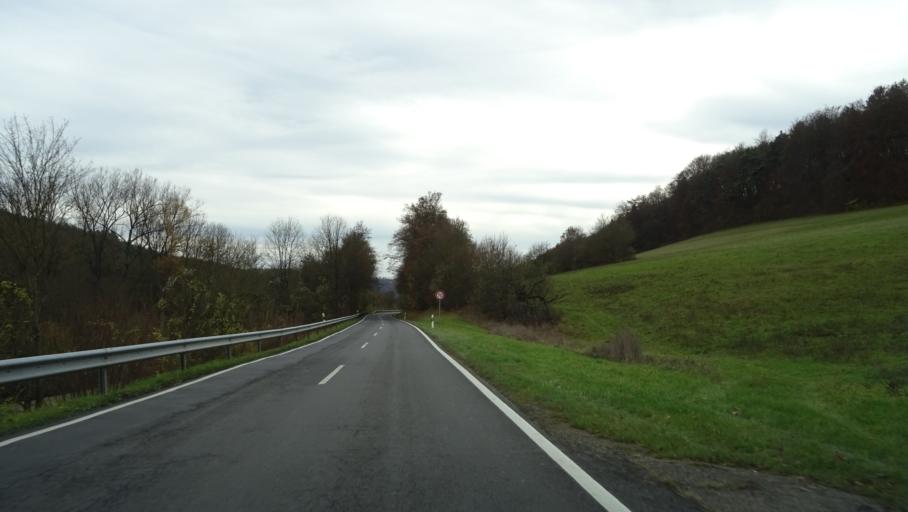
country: DE
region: Baden-Wuerttemberg
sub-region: Karlsruhe Region
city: Mosbach
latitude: 49.3635
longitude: 9.1269
